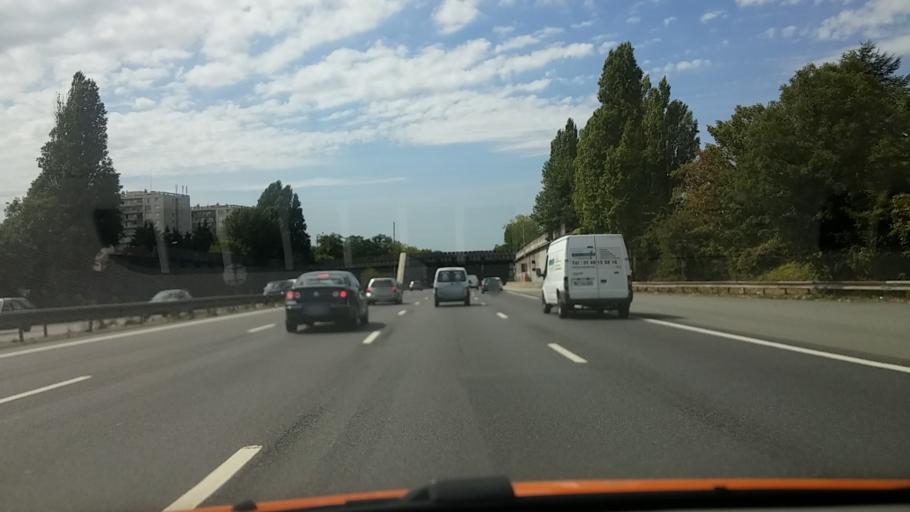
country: FR
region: Ile-de-France
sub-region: Departement du Val-de-Marne
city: Bry-sur-Marne
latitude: 48.8265
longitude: 2.5191
